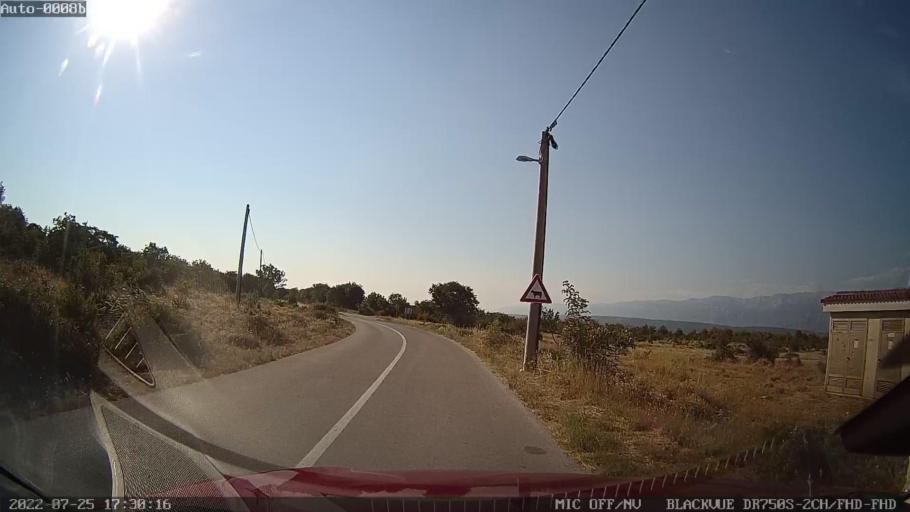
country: HR
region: Zadarska
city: Pridraga
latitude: 44.1638
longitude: 15.5104
